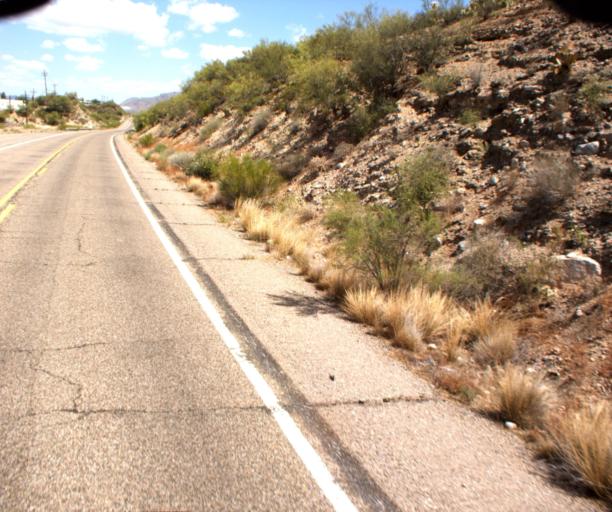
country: US
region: Arizona
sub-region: Pinal County
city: Kearny
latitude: 33.0779
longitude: -110.9236
